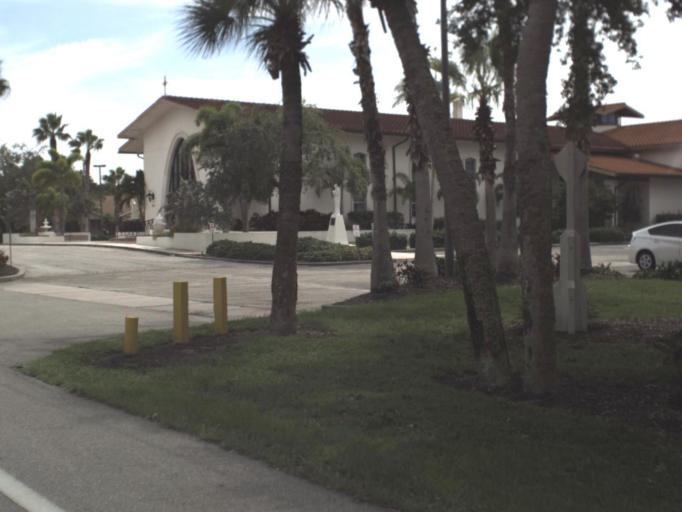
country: US
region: Florida
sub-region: Sarasota County
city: South Sarasota
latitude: 27.2746
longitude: -82.5473
